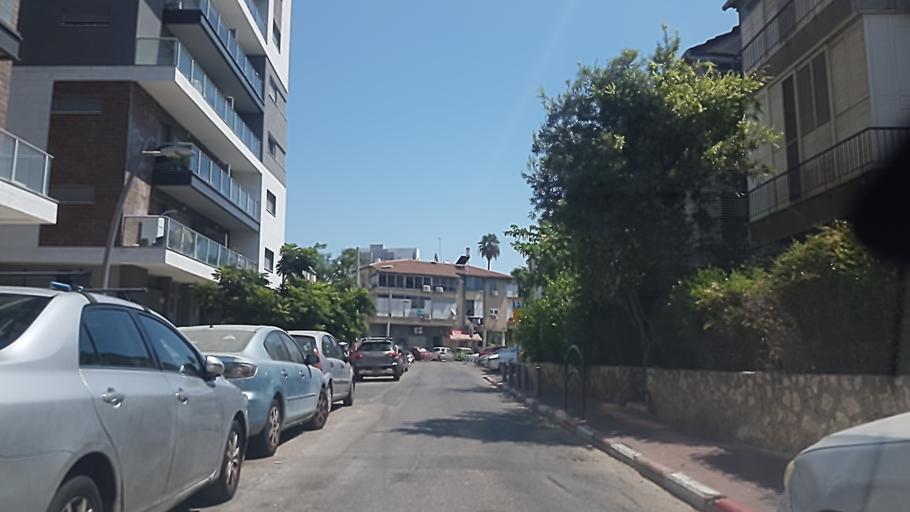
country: IL
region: Tel Aviv
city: Bene Beraq
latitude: 32.0837
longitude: 34.8251
